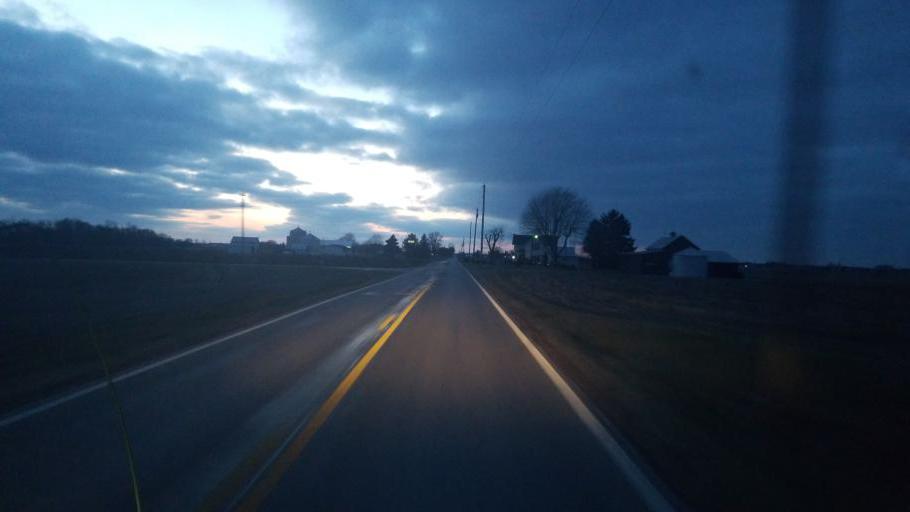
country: US
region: Ohio
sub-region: Marion County
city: Prospect
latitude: 40.4309
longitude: -83.1410
